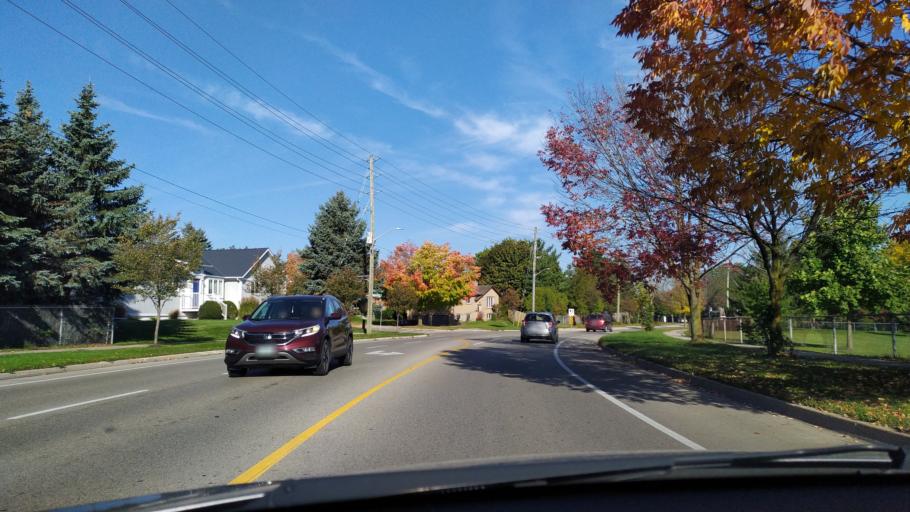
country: CA
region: Ontario
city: Waterloo
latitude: 43.4933
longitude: -80.5131
